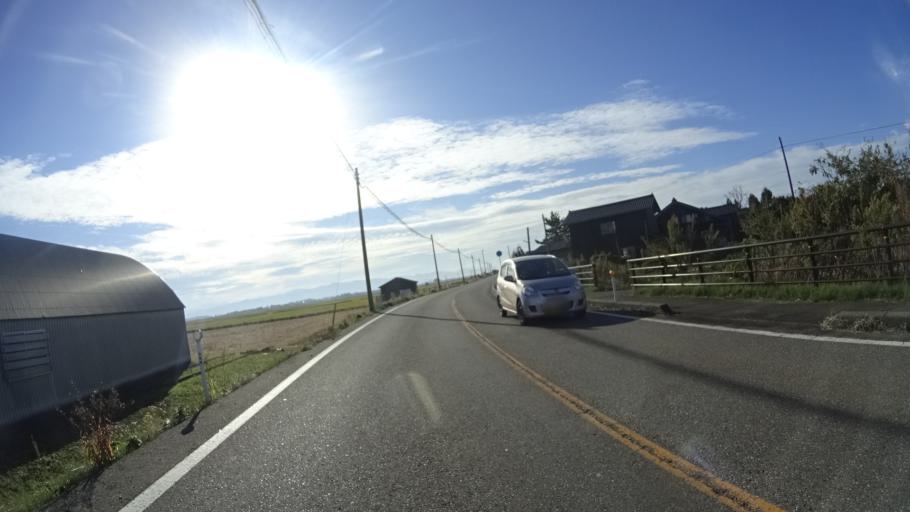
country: JP
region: Niigata
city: Mitsuke
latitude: 37.5737
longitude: 138.8414
